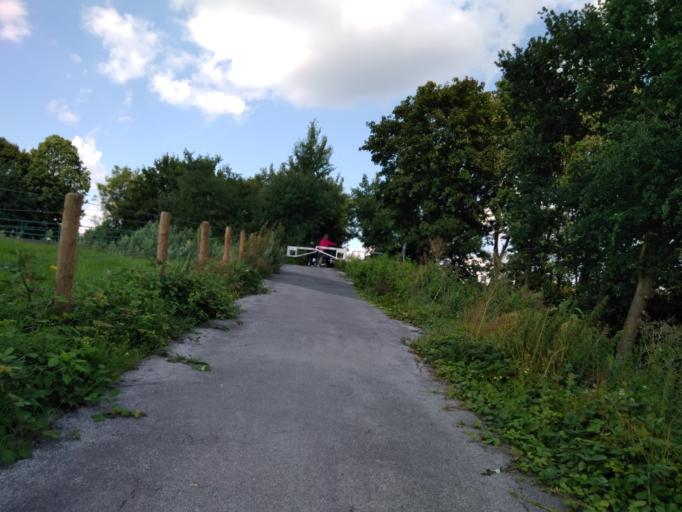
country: DE
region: North Rhine-Westphalia
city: Dorsten
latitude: 51.6626
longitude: 6.9764
